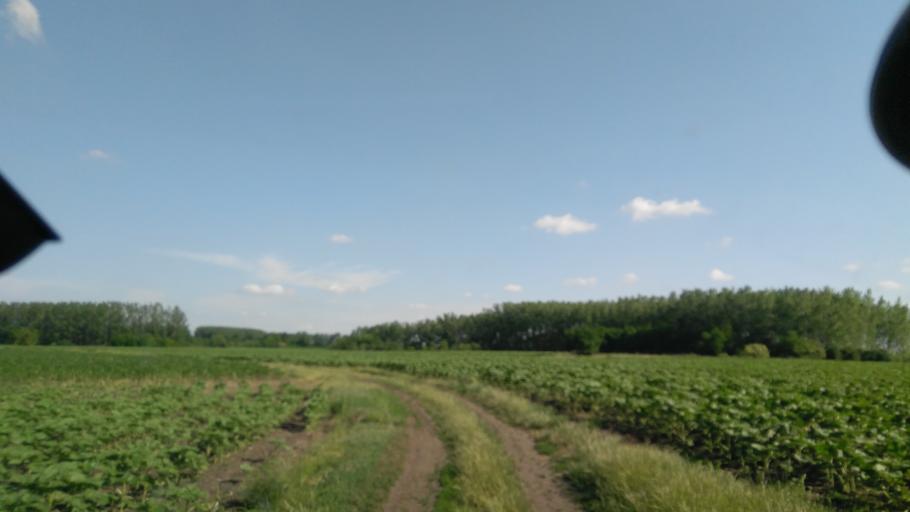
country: HU
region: Bekes
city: Doboz
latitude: 46.7027
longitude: 21.2340
